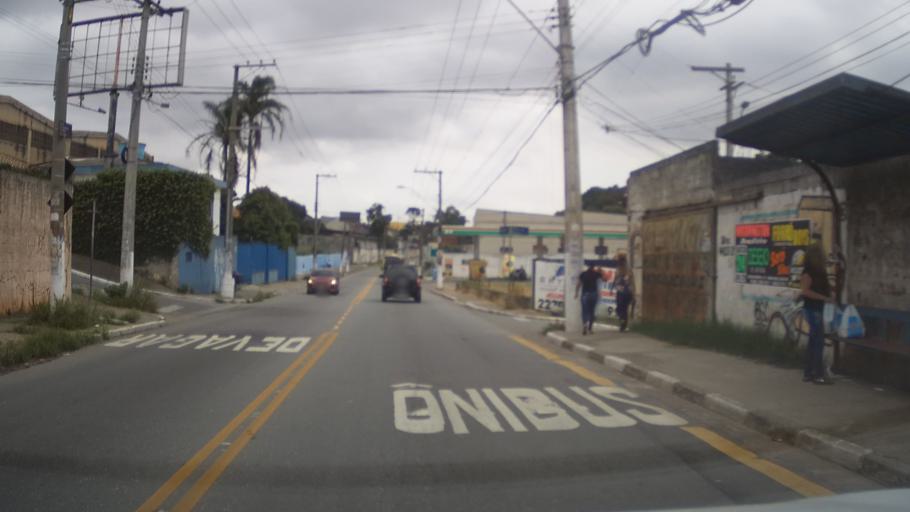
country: BR
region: Sao Paulo
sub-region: Itaquaquecetuba
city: Itaquaquecetuba
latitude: -23.4602
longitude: -46.4122
